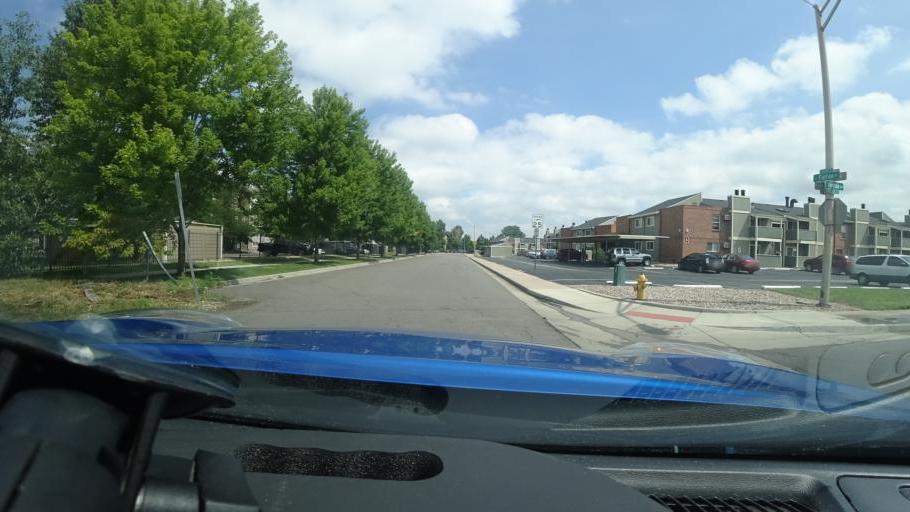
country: US
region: Colorado
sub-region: Adams County
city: Aurora
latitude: 39.7070
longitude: -104.8706
